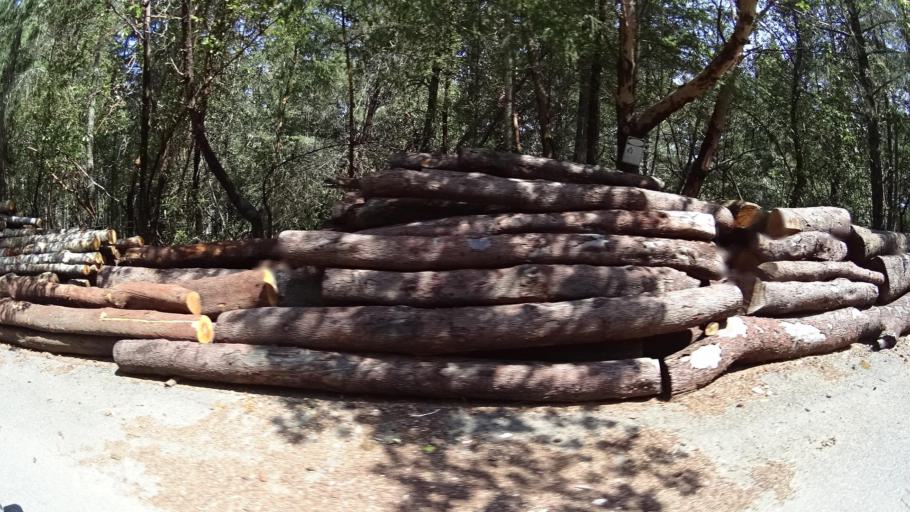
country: US
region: California
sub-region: Humboldt County
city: Redway
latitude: 40.1435
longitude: -123.6294
